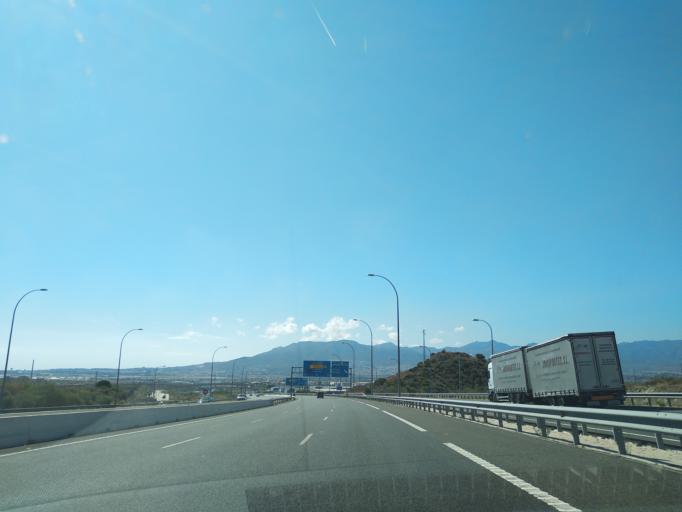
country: ES
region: Andalusia
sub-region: Provincia de Malaga
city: Alhaurin de la Torre
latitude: 36.7247
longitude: -4.5089
